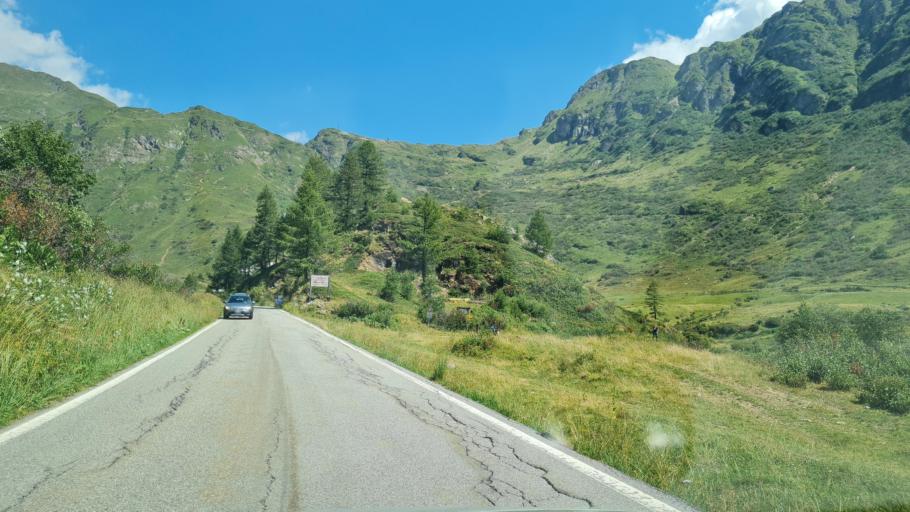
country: IT
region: Piedmont
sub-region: Provincia Verbano-Cusio-Ossola
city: Formazza
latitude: 46.4174
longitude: 8.4161
